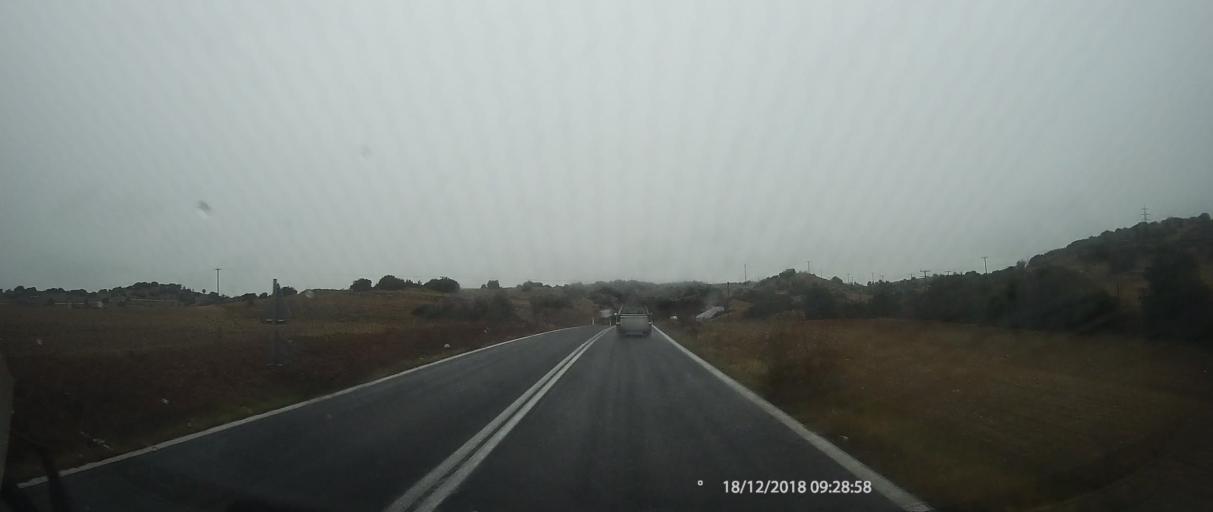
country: GR
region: Thessaly
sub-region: Nomos Larisis
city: Elassona
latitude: 39.9235
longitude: 22.1718
